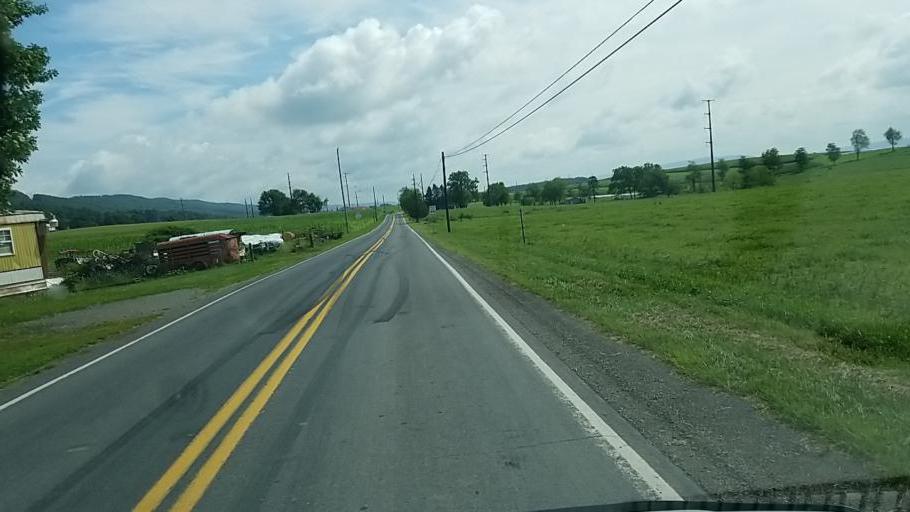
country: US
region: Pennsylvania
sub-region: Dauphin County
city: Millersburg
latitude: 40.5899
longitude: -76.9031
